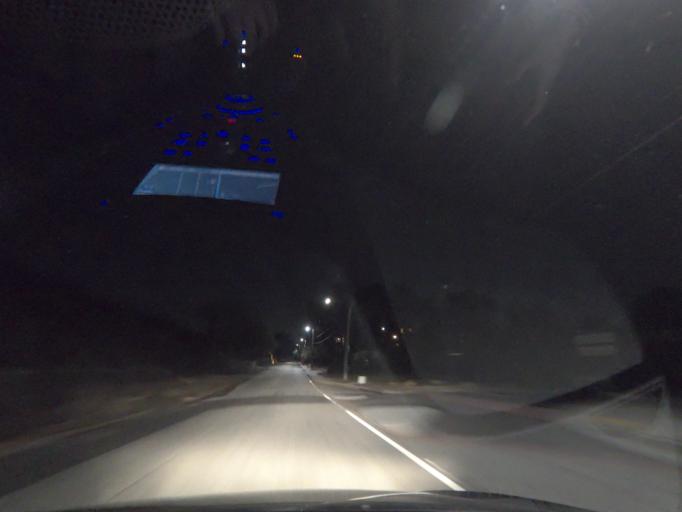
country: US
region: Georgia
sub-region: Cobb County
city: Vinings
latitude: 33.8102
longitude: -84.4540
